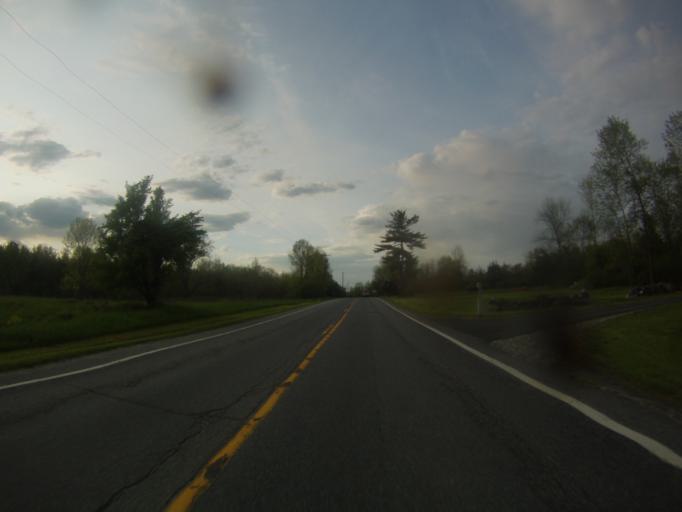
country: US
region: New York
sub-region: Essex County
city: Port Henry
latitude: 44.0085
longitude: -73.4195
